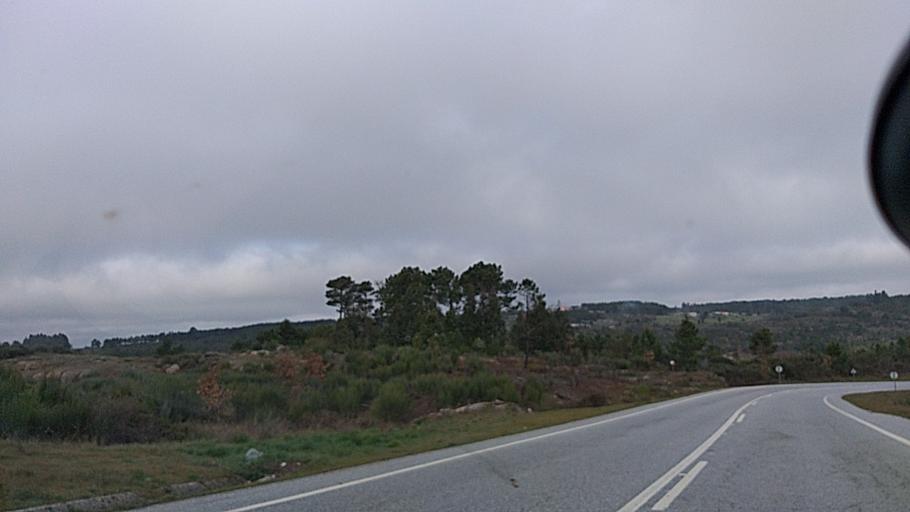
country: PT
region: Guarda
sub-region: Aguiar da Beira
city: Aguiar da Beira
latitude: 40.7743
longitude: -7.5050
